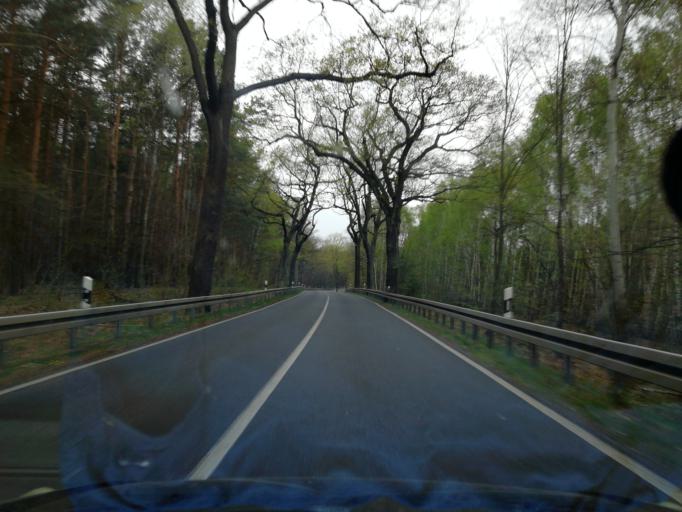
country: DE
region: Brandenburg
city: Calau
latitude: 51.7725
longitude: 13.8973
